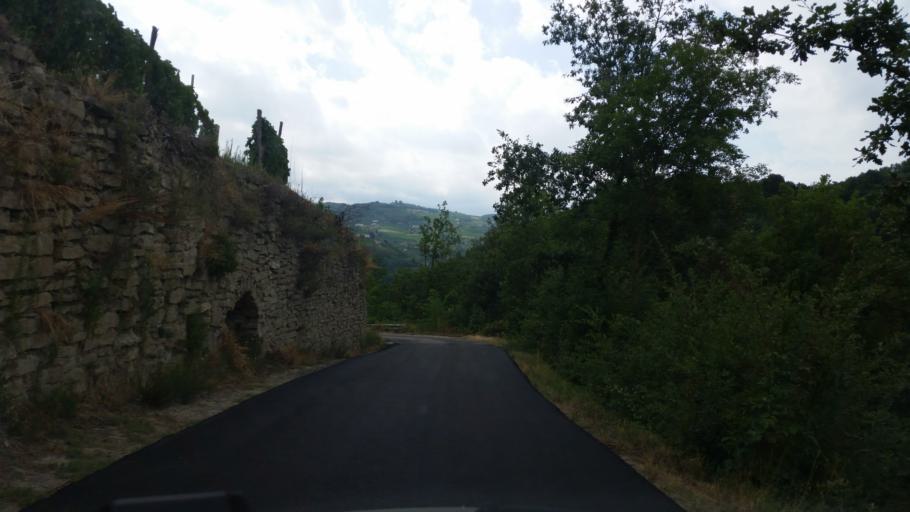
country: IT
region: Piedmont
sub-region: Provincia di Cuneo
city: Camo
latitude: 44.6875
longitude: 8.1907
